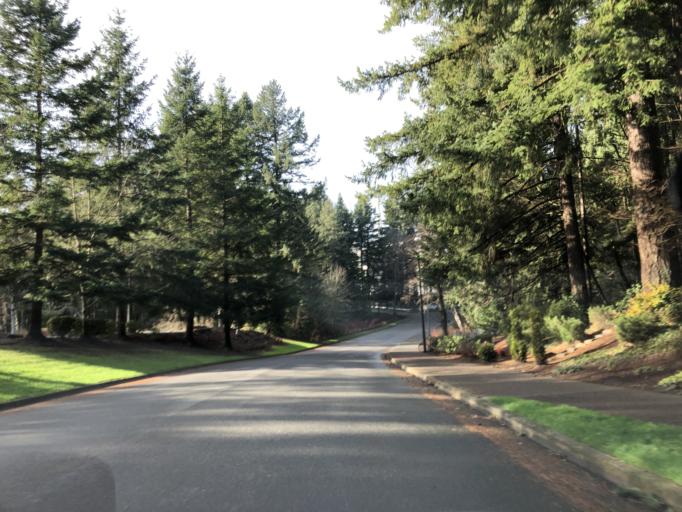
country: US
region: Oregon
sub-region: Washington County
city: Durham
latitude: 45.4242
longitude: -122.7392
